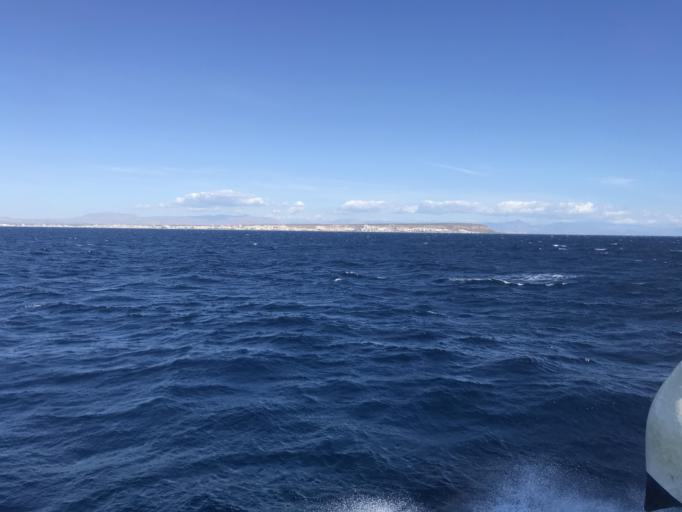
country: ES
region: Valencia
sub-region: Provincia de Alicante
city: Santa Pola
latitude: 38.1338
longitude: -0.5325
